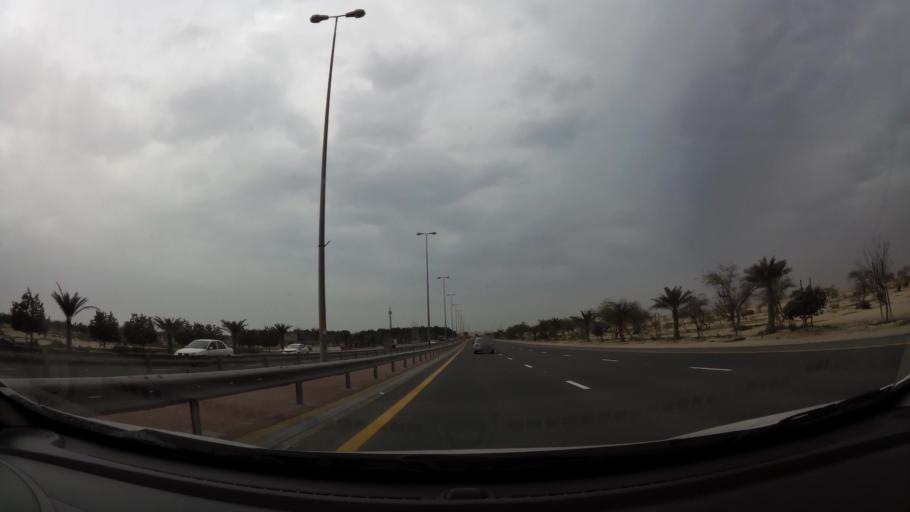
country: BH
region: Central Governorate
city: Dar Kulayb
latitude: 26.0745
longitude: 50.5324
